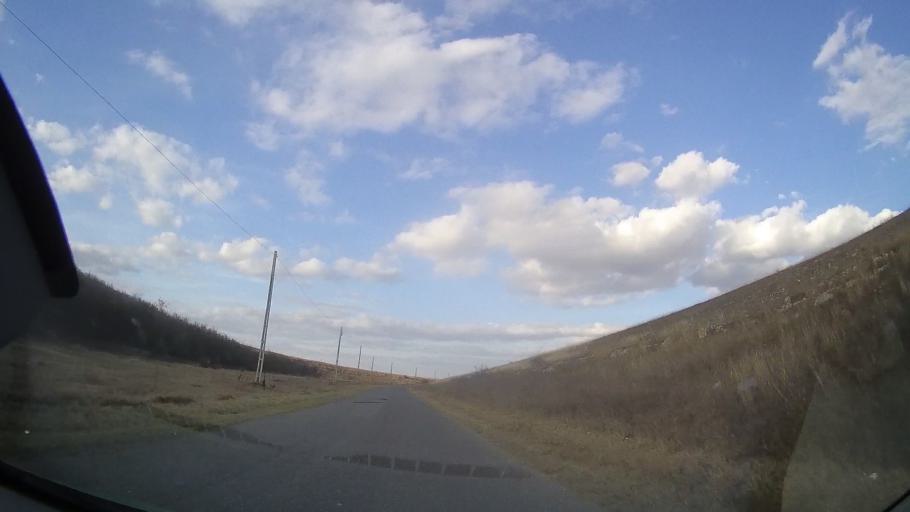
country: RO
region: Constanta
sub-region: Comuna Cerchezu
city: Cerchezu
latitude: 43.8363
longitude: 28.0975
